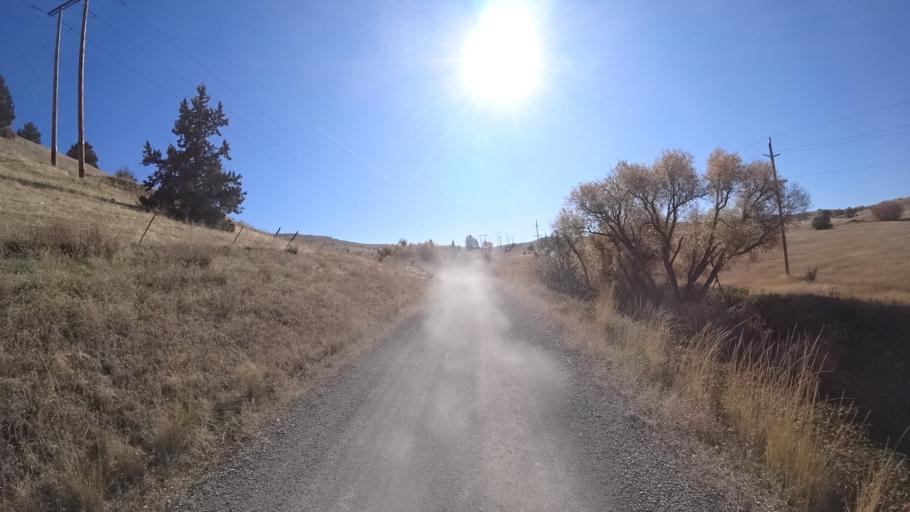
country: US
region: California
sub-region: Siskiyou County
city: Montague
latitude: 41.7880
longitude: -122.3592
